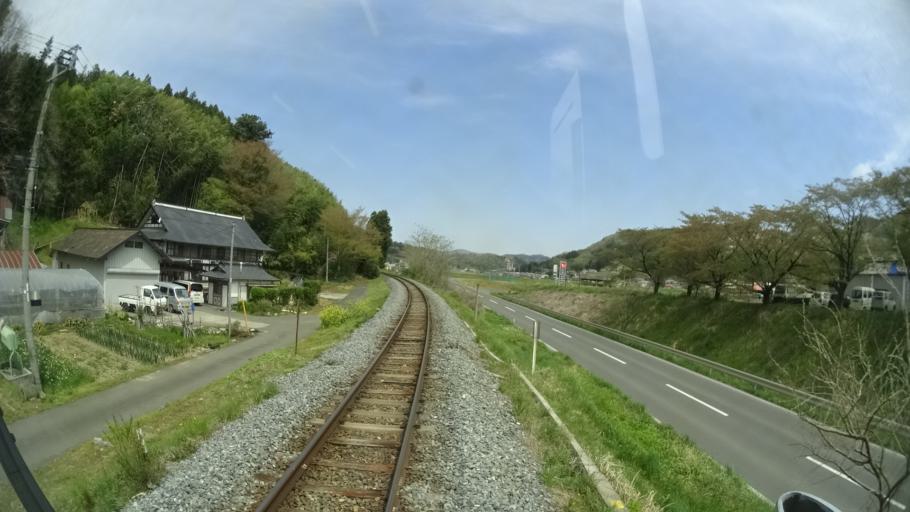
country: JP
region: Iwate
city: Ichinoseki
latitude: 38.9691
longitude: 141.2403
